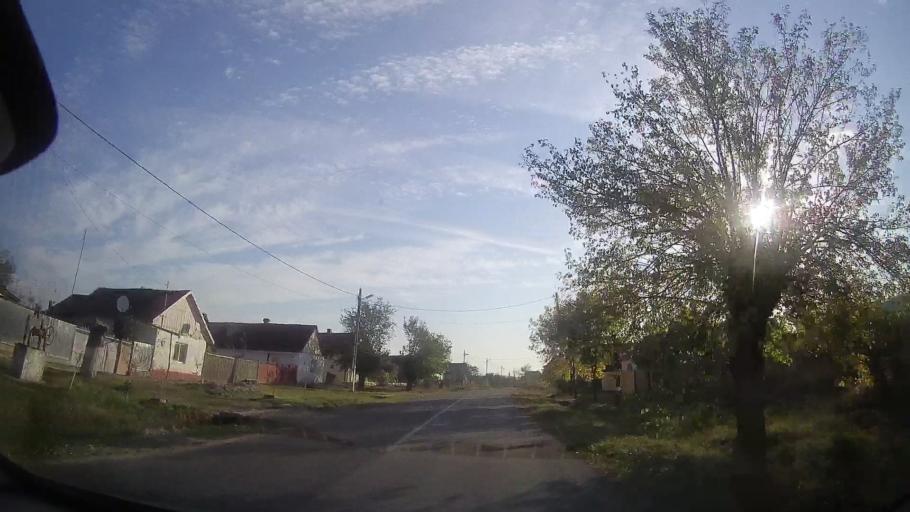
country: RO
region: Timis
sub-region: Comuna Bogda
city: Bogda
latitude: 45.9807
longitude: 21.5215
